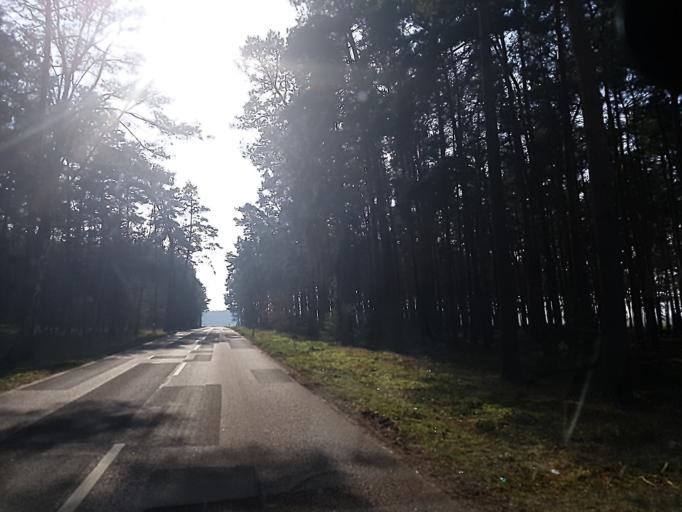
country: DE
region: Brandenburg
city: Wenzlow
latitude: 52.3110
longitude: 12.4406
